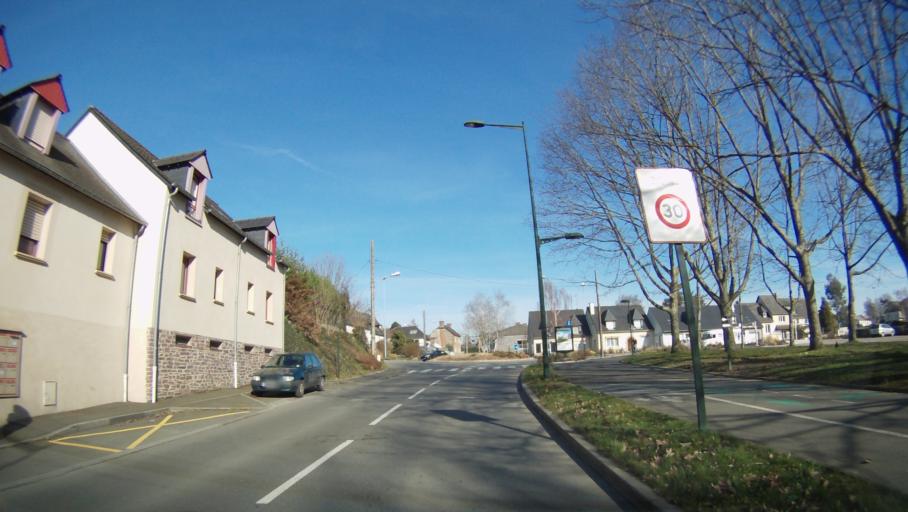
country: FR
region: Brittany
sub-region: Departement d'Ille-et-Vilaine
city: Chatillon-sur-Seiche
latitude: 48.0390
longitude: -1.6669
